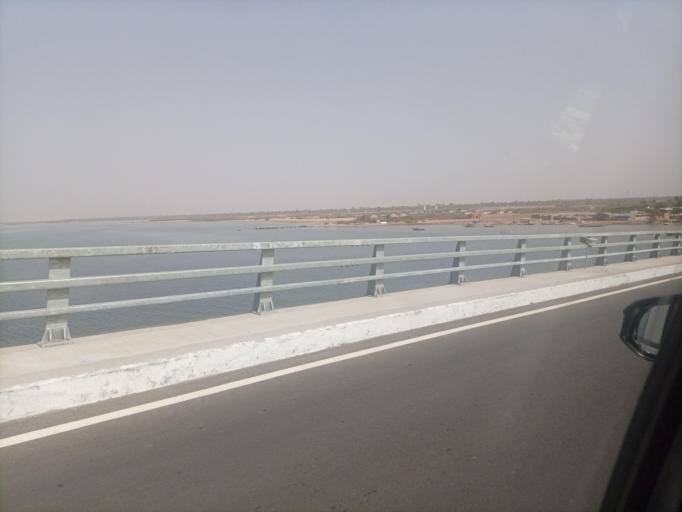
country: SN
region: Fatick
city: Foundiougne
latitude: 14.1328
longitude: -16.4673
